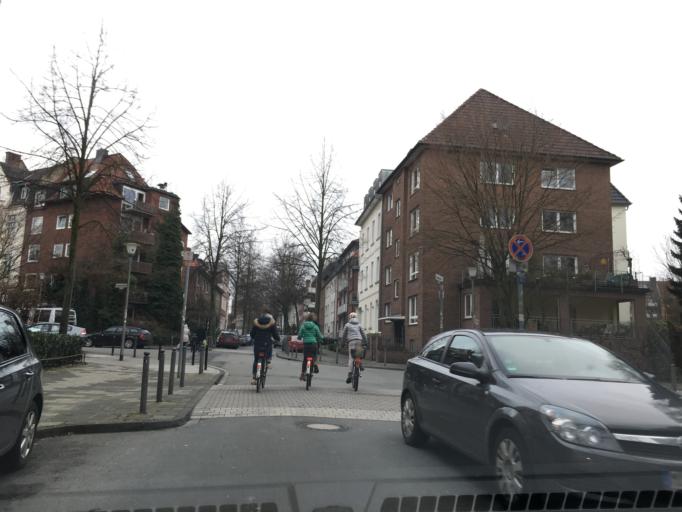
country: DE
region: North Rhine-Westphalia
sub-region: Regierungsbezirk Munster
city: Muenster
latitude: 51.9700
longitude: 7.6264
